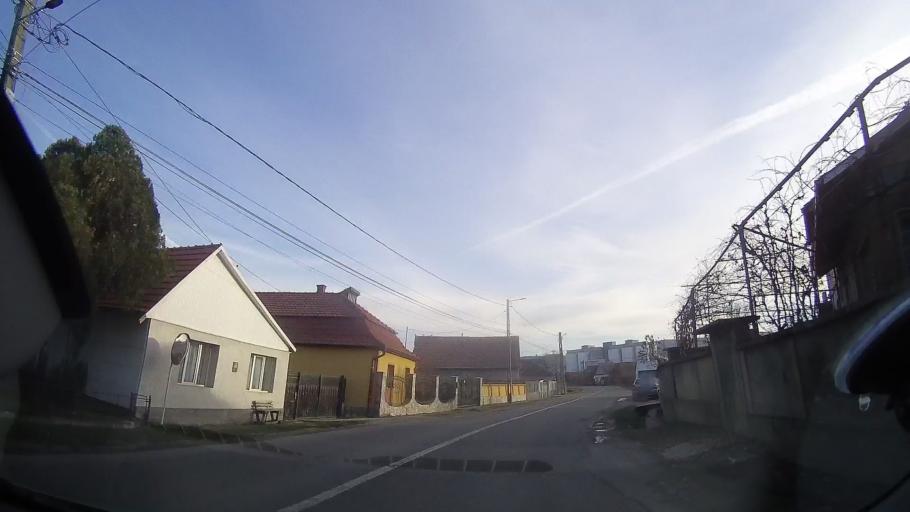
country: RO
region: Bihor
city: Lugasu de Jos
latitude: 47.0457
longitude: 22.3314
